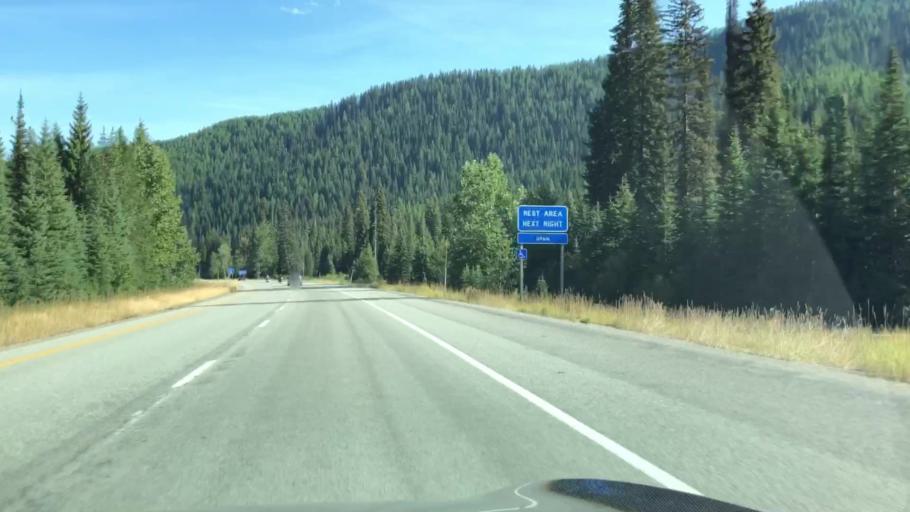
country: US
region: Idaho
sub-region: Shoshone County
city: Wallace
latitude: 47.4239
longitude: -115.6363
